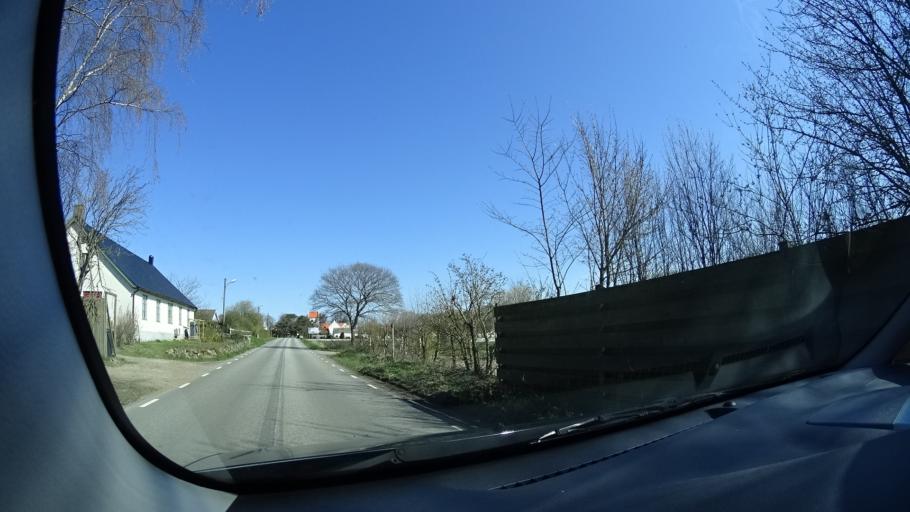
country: SE
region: Skane
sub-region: Hoganas Kommun
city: Hoganas
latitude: 56.2564
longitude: 12.5714
